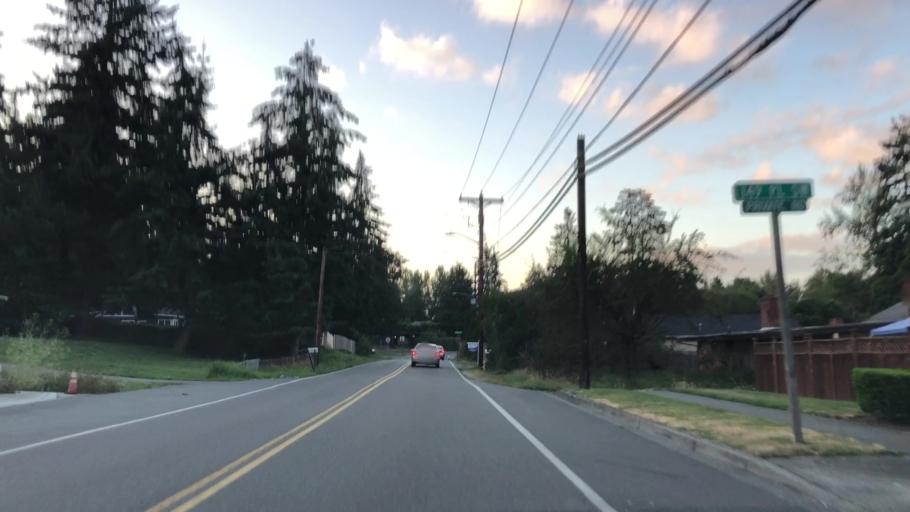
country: US
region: Washington
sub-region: Snohomish County
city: Martha Lake
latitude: 47.8631
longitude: -122.2687
